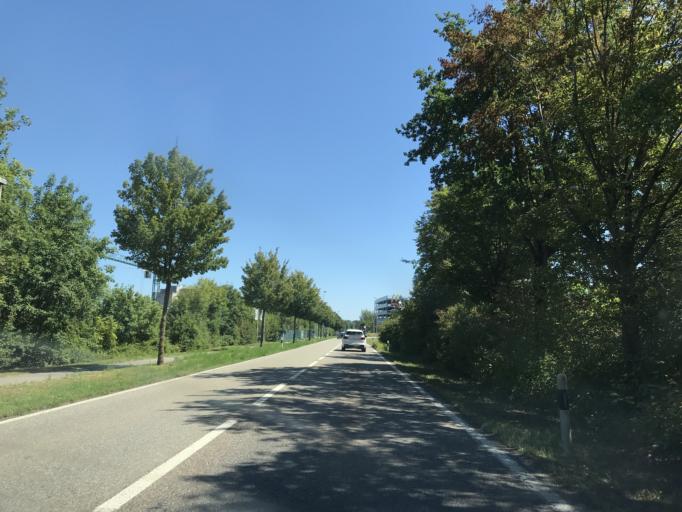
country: CH
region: Aargau
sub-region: Bezirk Rheinfelden
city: Kaiseraugst
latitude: 47.5386
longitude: 7.7316
